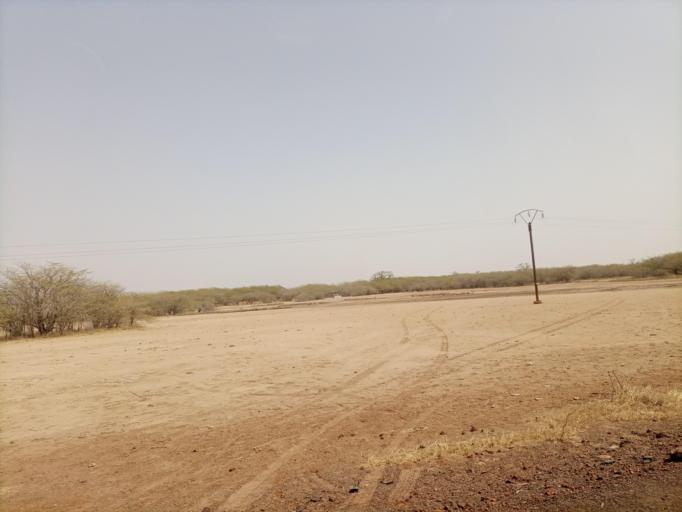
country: SN
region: Fatick
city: Foundiougne
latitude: 14.1862
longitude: -16.4546
